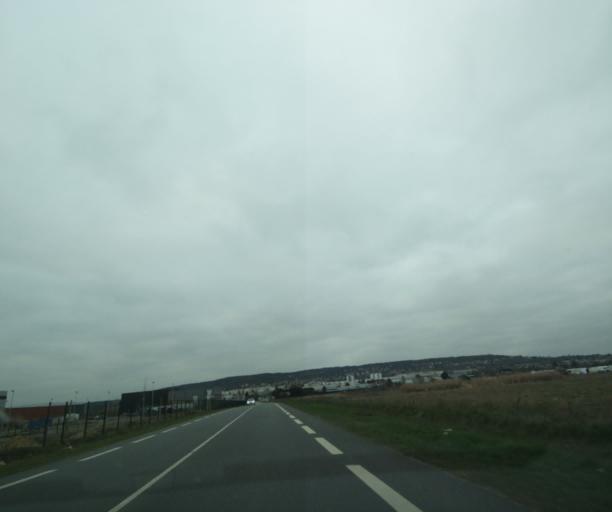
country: FR
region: Ile-de-France
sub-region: Departement des Yvelines
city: Carrieres-sous-Poissy
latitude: 48.9617
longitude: 2.0353
